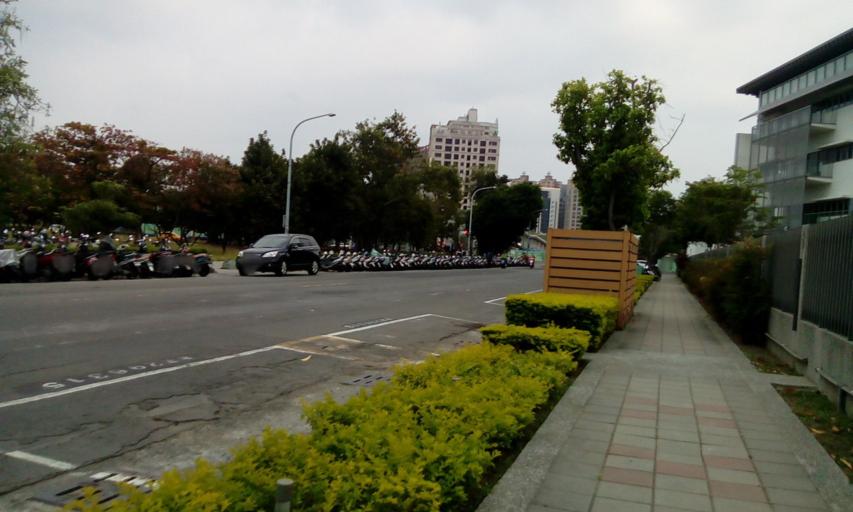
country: TW
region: Kaohsiung
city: Kaohsiung
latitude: 22.6766
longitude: 120.2937
